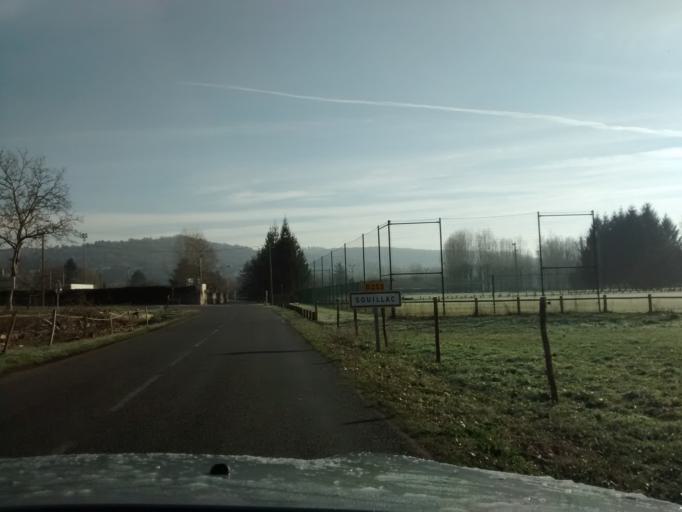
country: FR
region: Midi-Pyrenees
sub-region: Departement du Lot
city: Souillac
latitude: 44.8910
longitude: 1.4672
